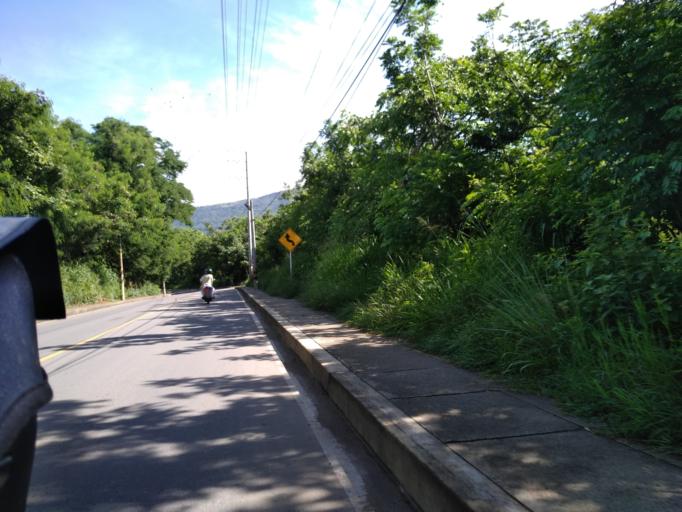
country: CO
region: Santander
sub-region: San Gil
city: San Gil
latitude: 6.5454
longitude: -73.1279
